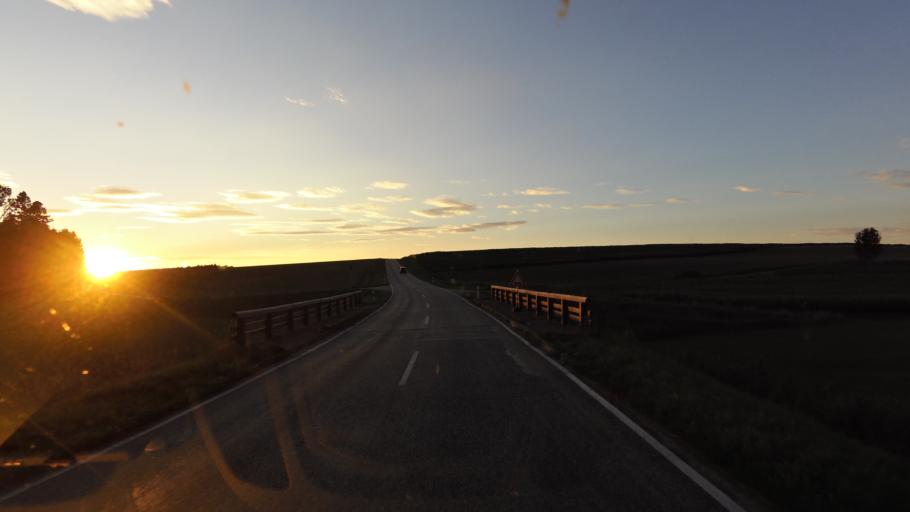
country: DE
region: Bavaria
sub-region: Upper Bavaria
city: Kienberg
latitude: 48.0985
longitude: 12.4776
